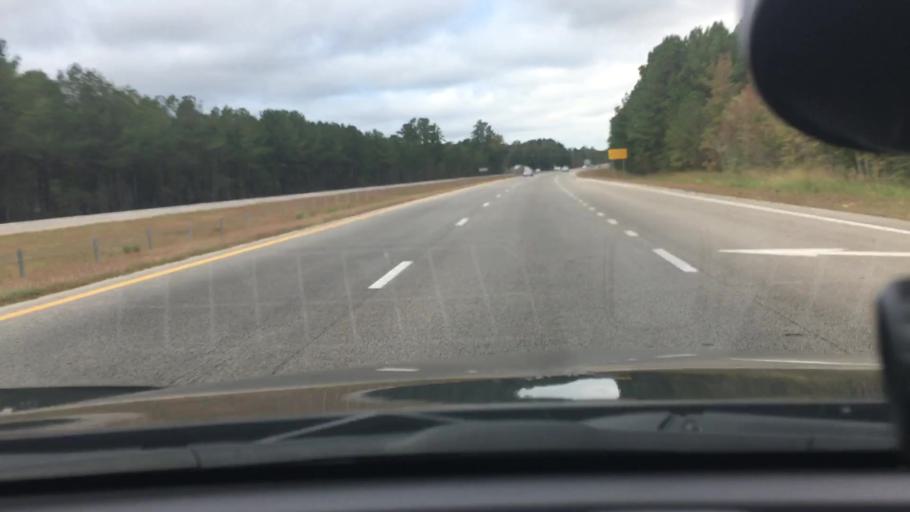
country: US
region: North Carolina
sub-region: Wilson County
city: Lucama
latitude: 35.7399
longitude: -78.0166
